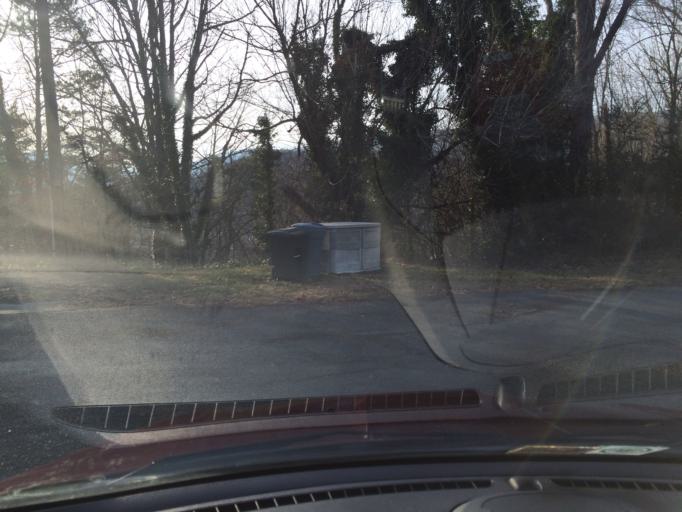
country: US
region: Virginia
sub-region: Alleghany County
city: Clifton Forge
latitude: 37.8193
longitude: -79.8208
